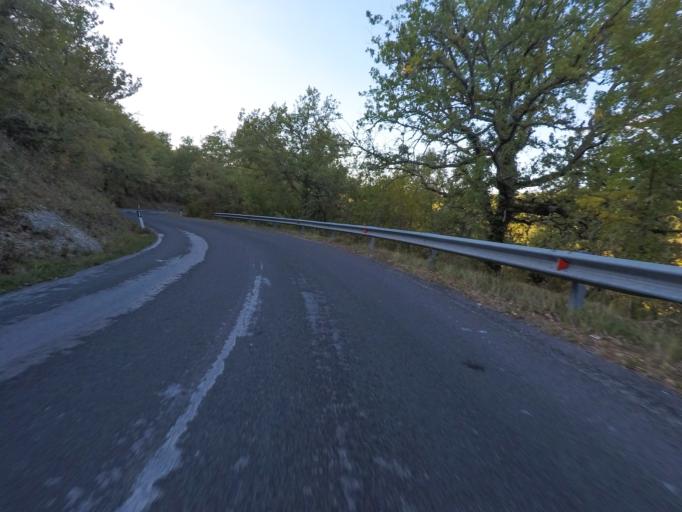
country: IT
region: Tuscany
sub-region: Provincia di Siena
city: Radda in Chianti
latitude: 43.4627
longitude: 11.3848
